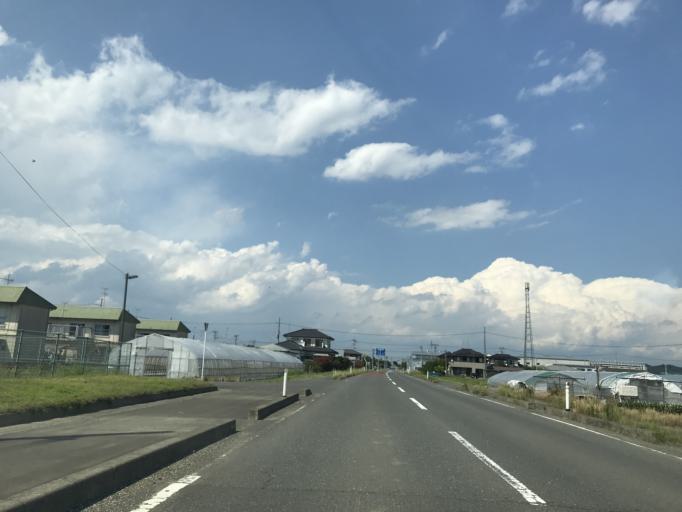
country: JP
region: Miyagi
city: Wakuya
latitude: 38.4681
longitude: 141.1304
